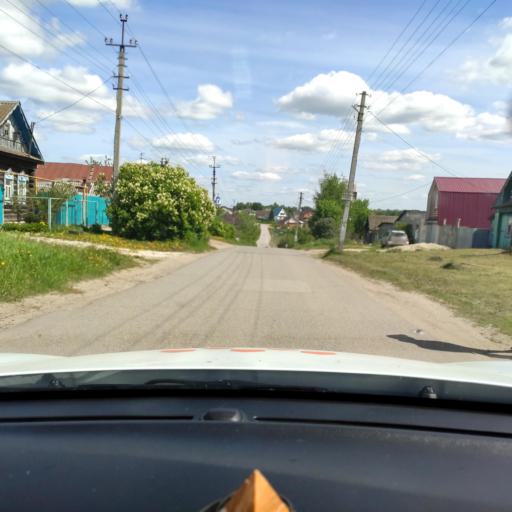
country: RU
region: Tatarstan
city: Osinovo
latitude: 55.8816
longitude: 48.8728
